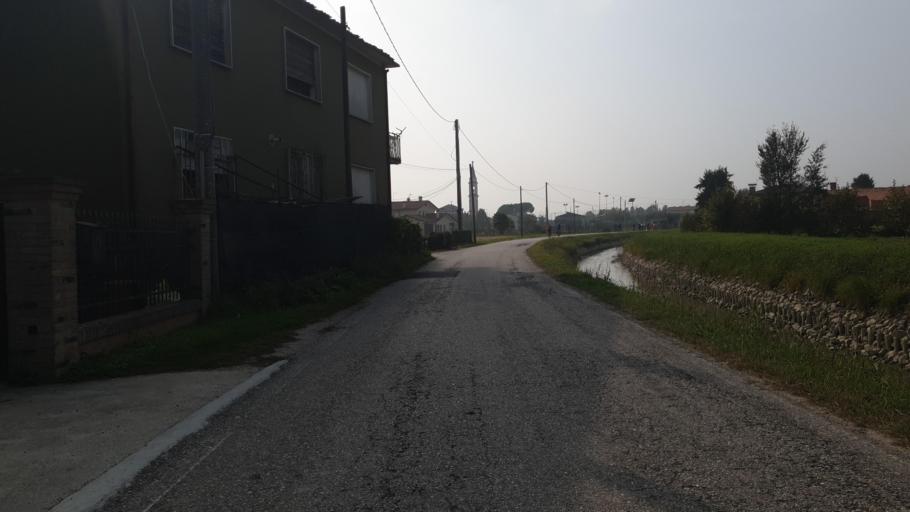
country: IT
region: Veneto
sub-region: Provincia di Padova
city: Vallonga
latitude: 45.2904
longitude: 12.0843
